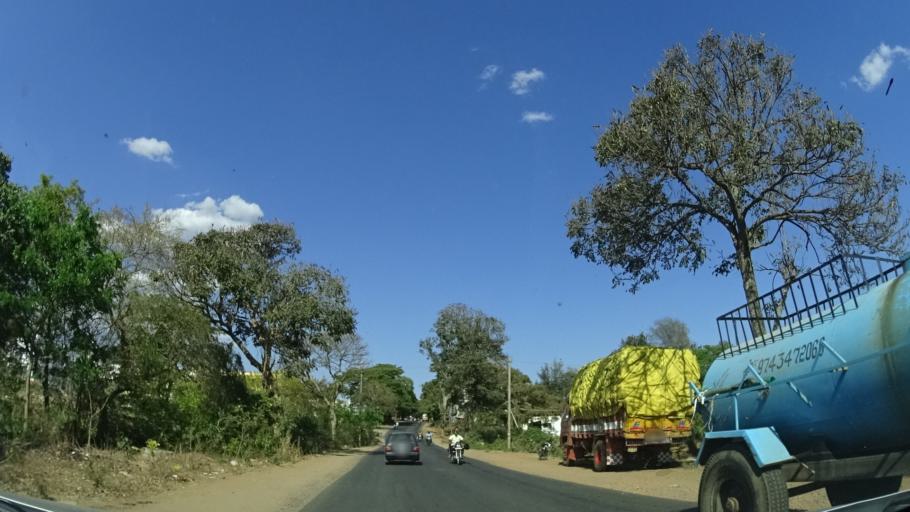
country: IN
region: Karnataka
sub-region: Chikmagalur
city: Chikmagalur
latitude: 13.3352
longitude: 75.7991
